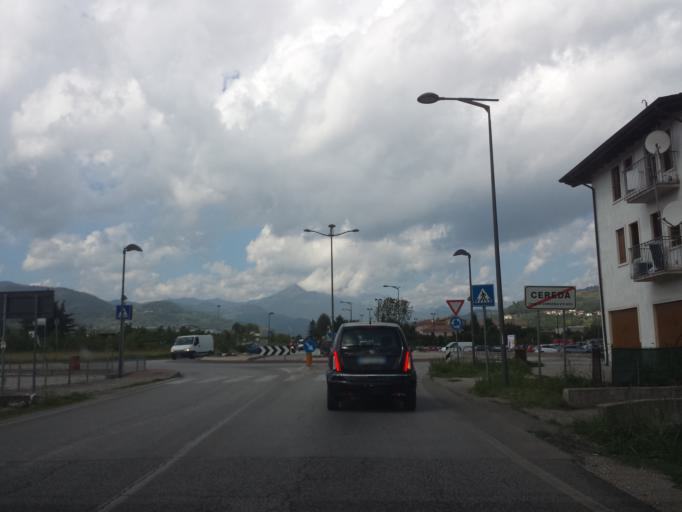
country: IT
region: Veneto
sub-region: Provincia di Vicenza
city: Cereda-Cozza Cornedo
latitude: 45.5986
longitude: 11.3662
